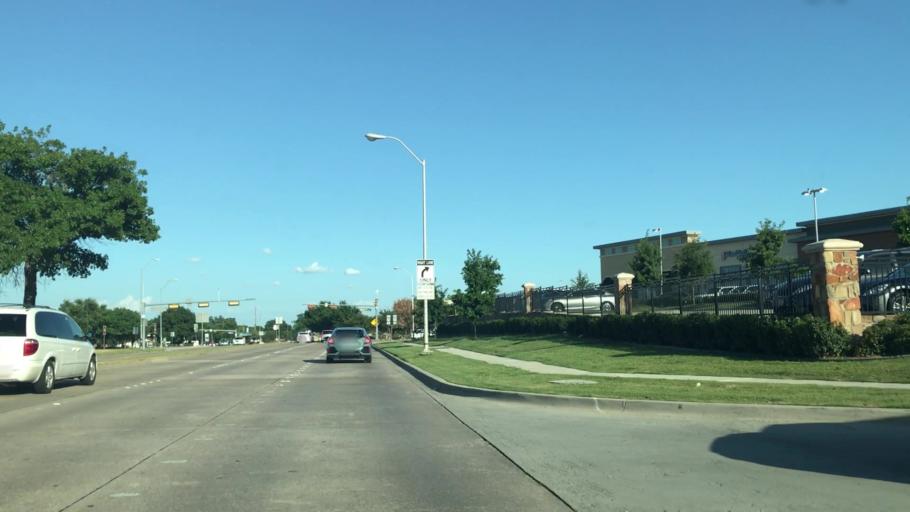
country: US
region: Texas
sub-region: Collin County
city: Allen
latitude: 33.0673
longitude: -96.6928
